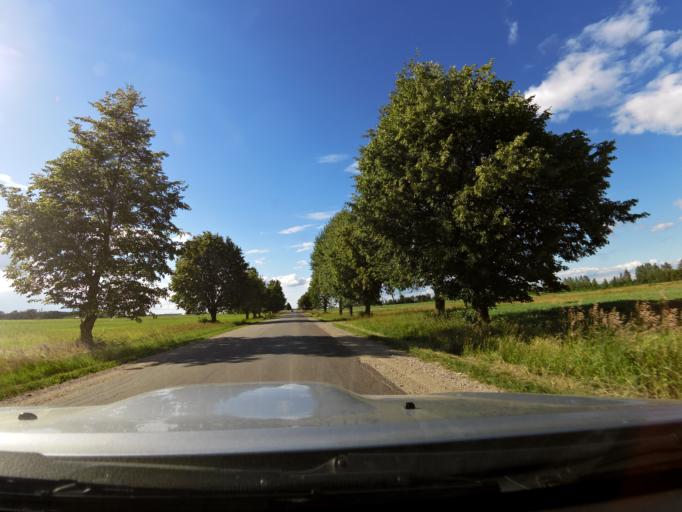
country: LT
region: Panevezys
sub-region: Birzai
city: Birzai
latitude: 56.2490
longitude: 24.8501
